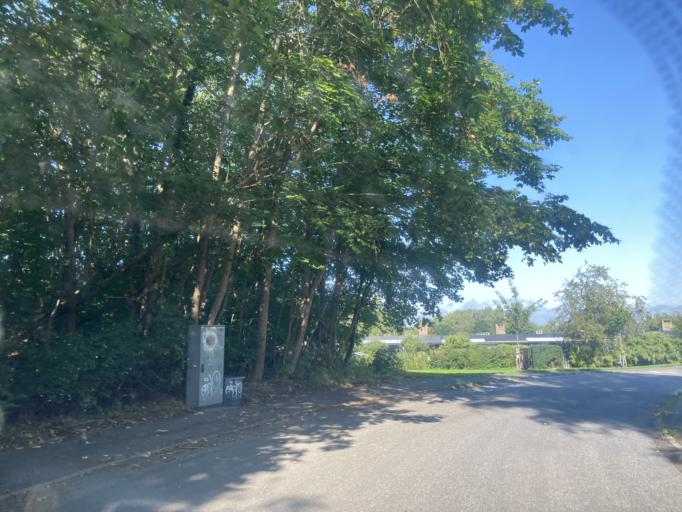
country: DK
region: Capital Region
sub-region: Fredensborg Kommune
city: Kokkedal
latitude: 55.9051
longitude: 12.5026
